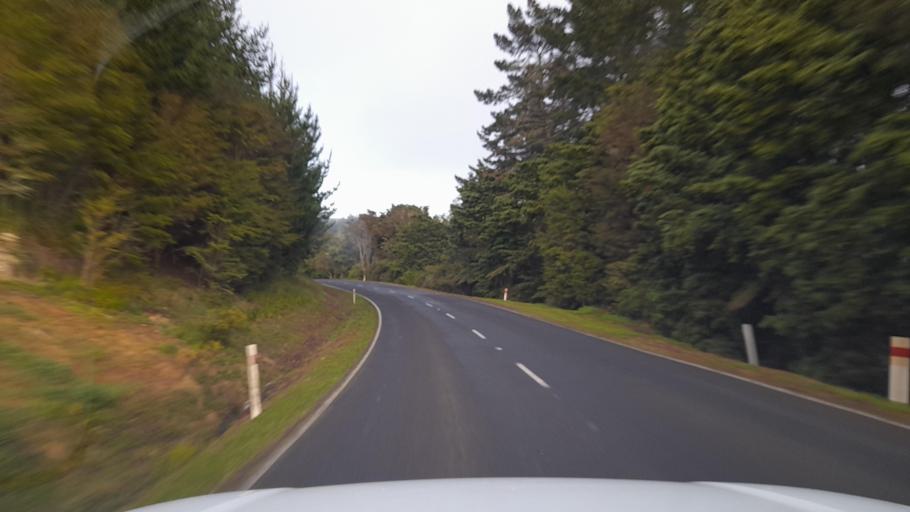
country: NZ
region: Northland
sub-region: Kaipara District
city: Dargaville
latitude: -35.7068
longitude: 173.9332
